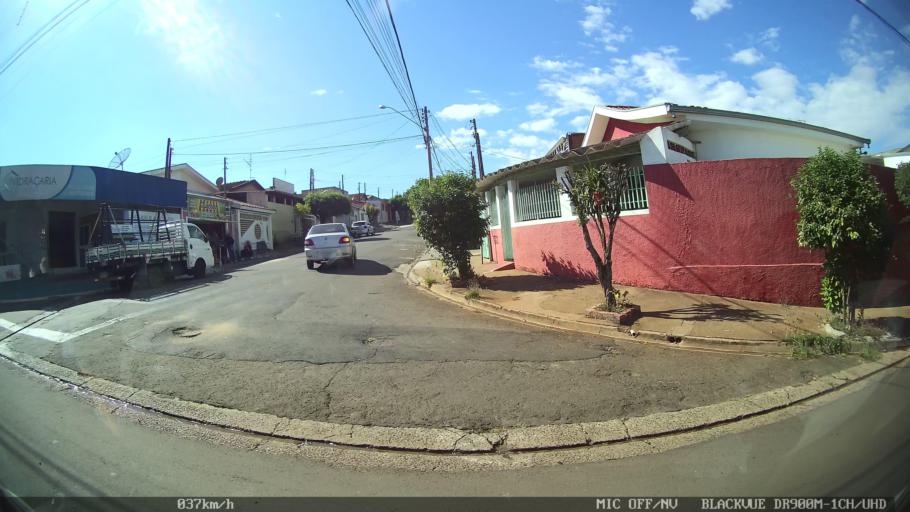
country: BR
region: Sao Paulo
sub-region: Santa Barbara D'Oeste
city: Santa Barbara d'Oeste
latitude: -22.7363
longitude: -47.3904
